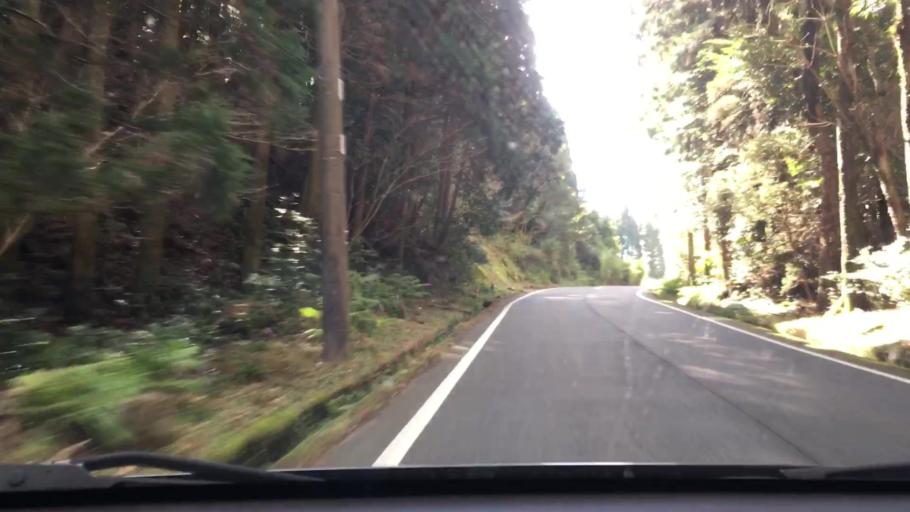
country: JP
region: Kagoshima
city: Ijuin
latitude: 31.7170
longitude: 130.4278
